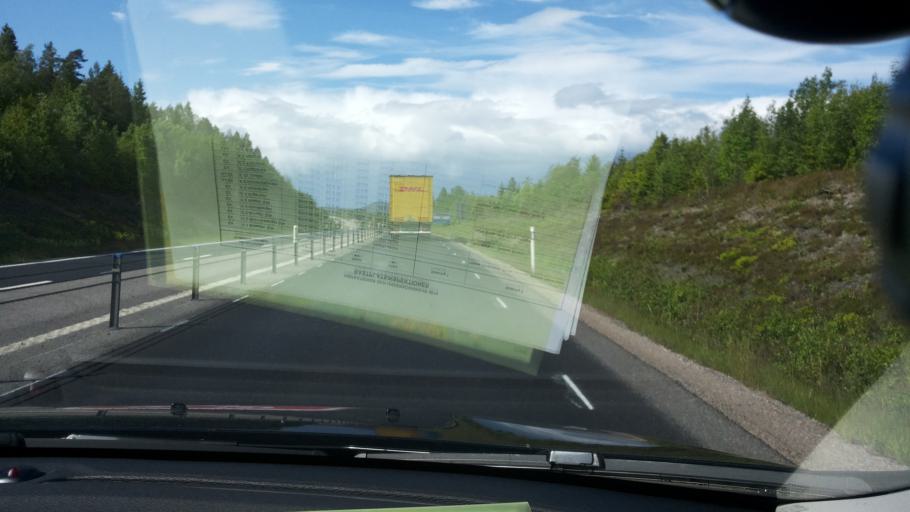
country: SE
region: Vaesternorrland
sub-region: Sundsvalls Kommun
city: Njurundabommen
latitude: 62.2362
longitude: 17.3751
